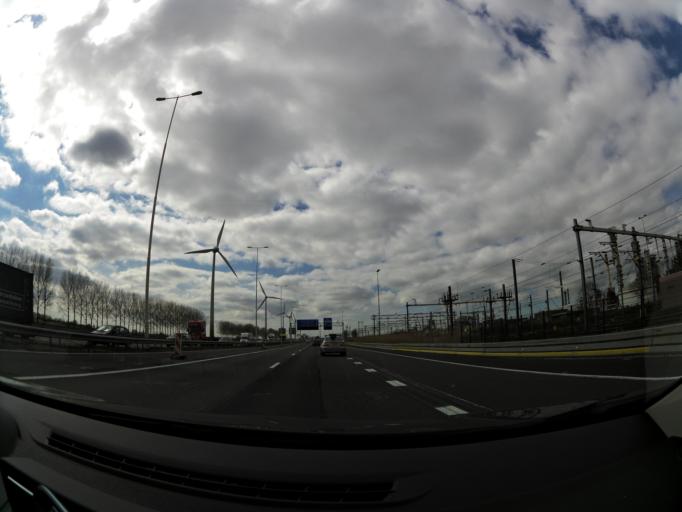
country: NL
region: South Holland
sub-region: Gemeente Spijkenisse
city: Spijkenisse
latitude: 51.8681
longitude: 4.2951
